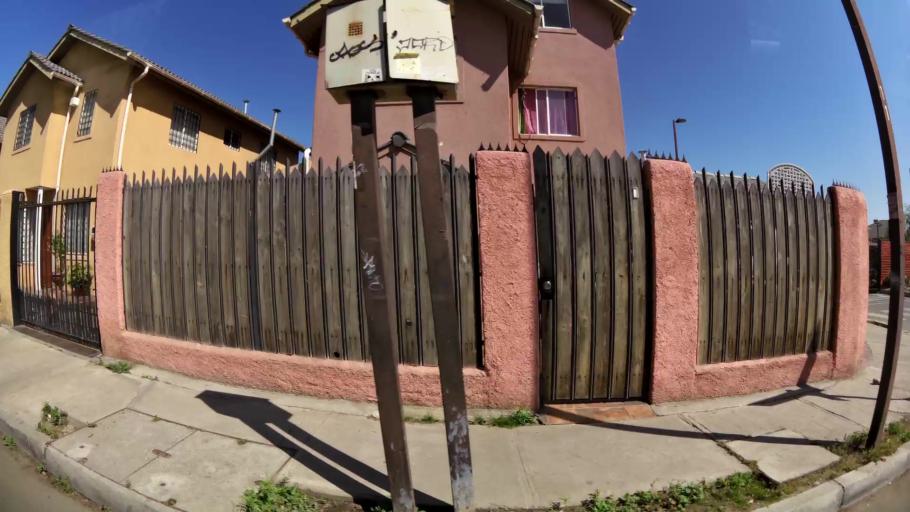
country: CL
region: Santiago Metropolitan
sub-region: Provincia de Chacabuco
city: Chicureo Abajo
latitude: -33.3275
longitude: -70.7467
